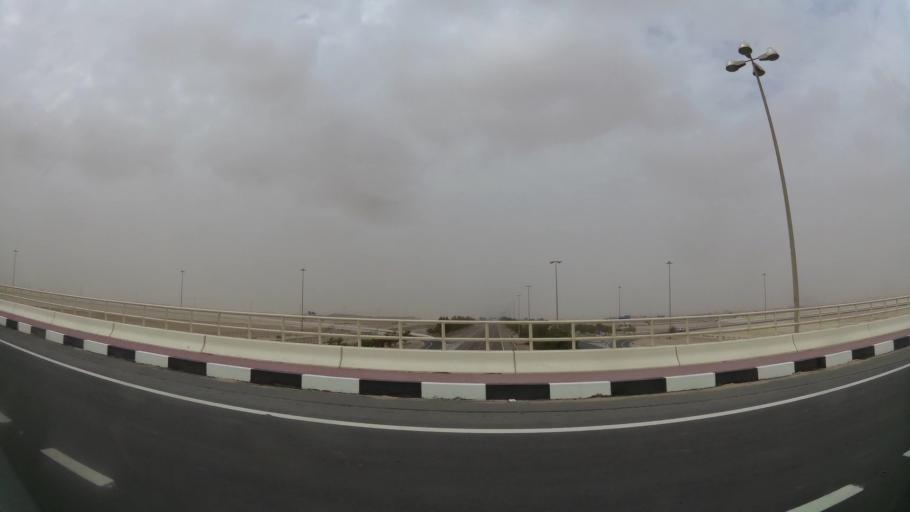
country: AE
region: Abu Dhabi
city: Abu Dhabi
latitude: 24.4145
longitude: 54.7145
